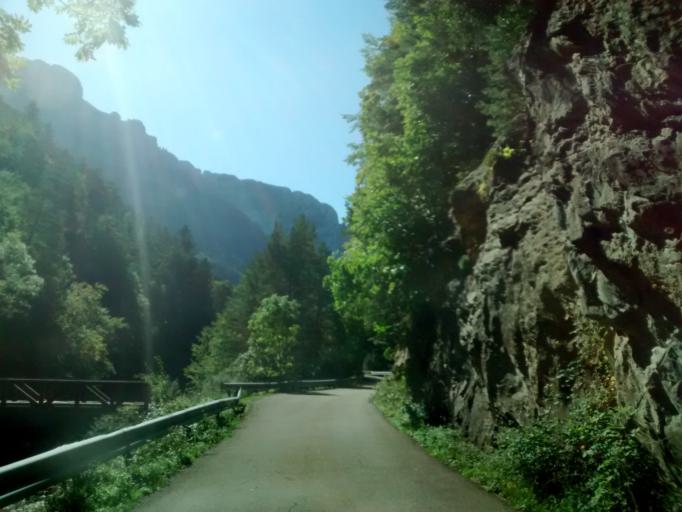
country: ES
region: Aragon
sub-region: Provincia de Huesca
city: Aragues del Puerto
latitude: 42.8215
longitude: -0.7116
